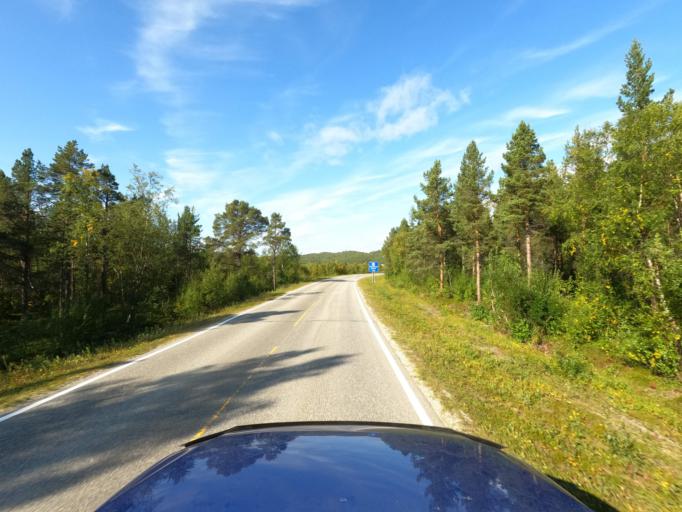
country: NO
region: Finnmark Fylke
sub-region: Porsanger
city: Lakselv
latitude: 69.8248
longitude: 25.1488
